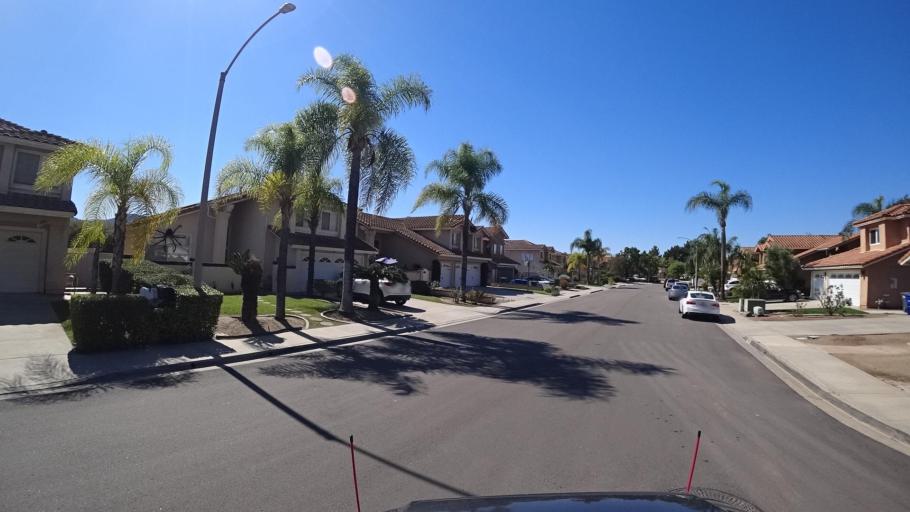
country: US
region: California
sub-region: San Diego County
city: Rancho San Diego
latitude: 32.7472
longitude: -116.9171
